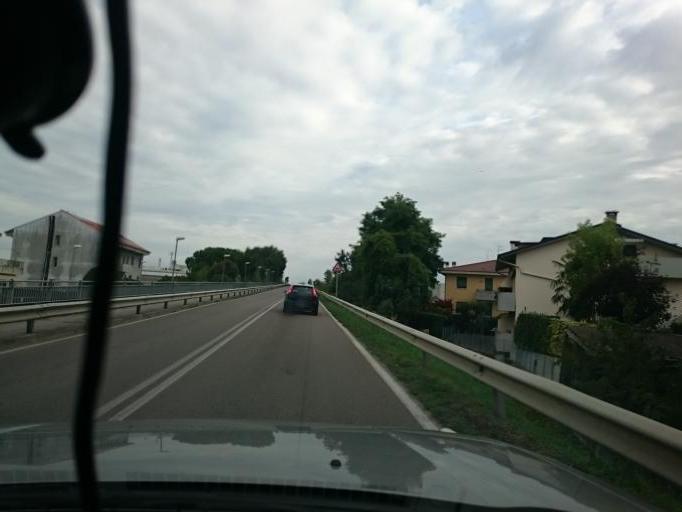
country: IT
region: Veneto
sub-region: Provincia di Vicenza
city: Grisignano di Zocco
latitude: 45.4772
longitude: 11.7032
